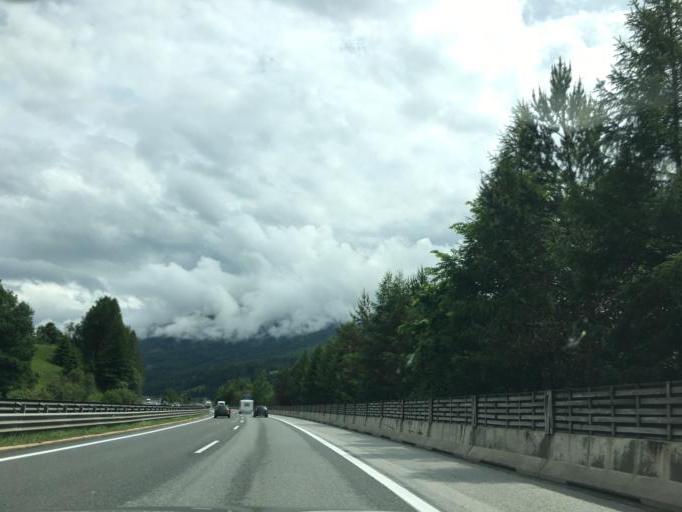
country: AT
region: Salzburg
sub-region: Politischer Bezirk Tamsweg
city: Sankt Michael im Lungau
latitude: 47.0999
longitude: 13.6014
